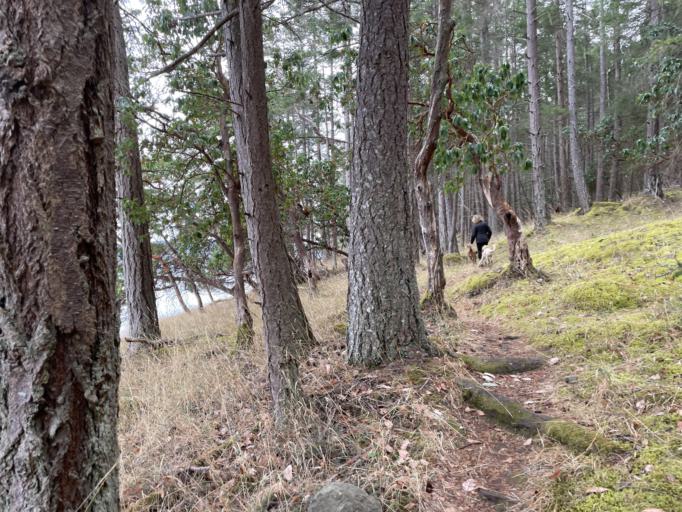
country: CA
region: British Columbia
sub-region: Cowichan Valley Regional District
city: Ladysmith
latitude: 49.0977
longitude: -123.7258
